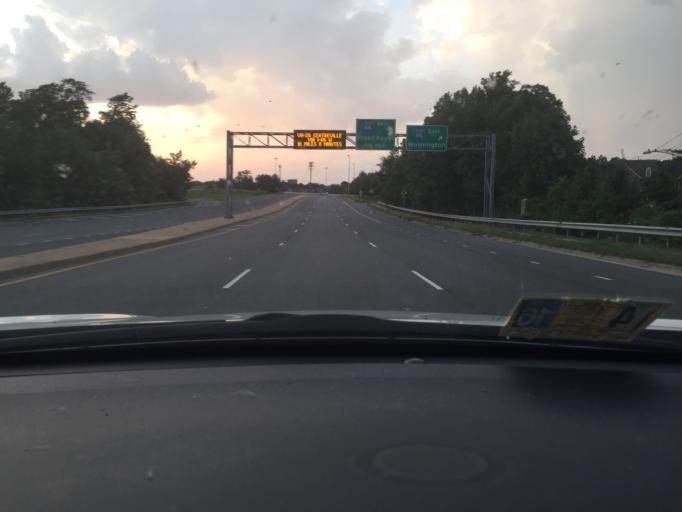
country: US
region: Virginia
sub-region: Fairfax County
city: Mantua
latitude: 38.8752
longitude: -77.2645
